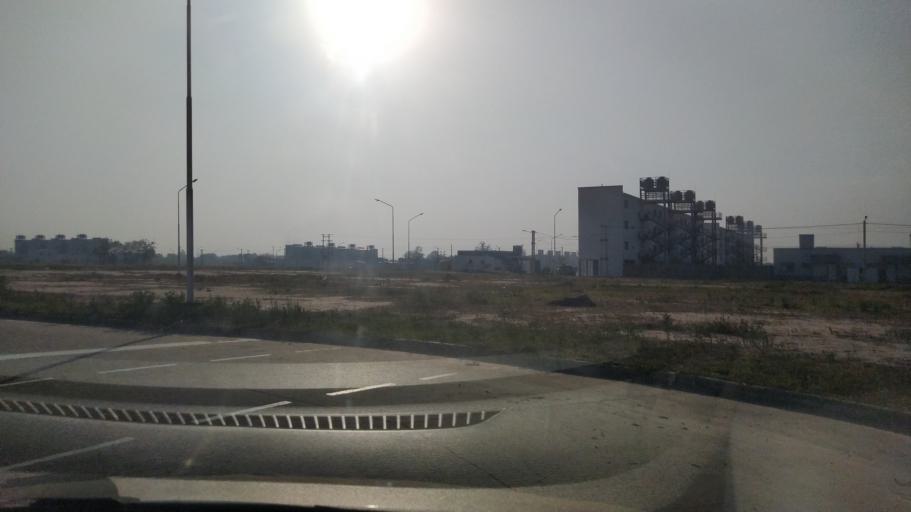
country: AR
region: Corrientes
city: Corrientes
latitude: -27.5266
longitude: -58.8057
